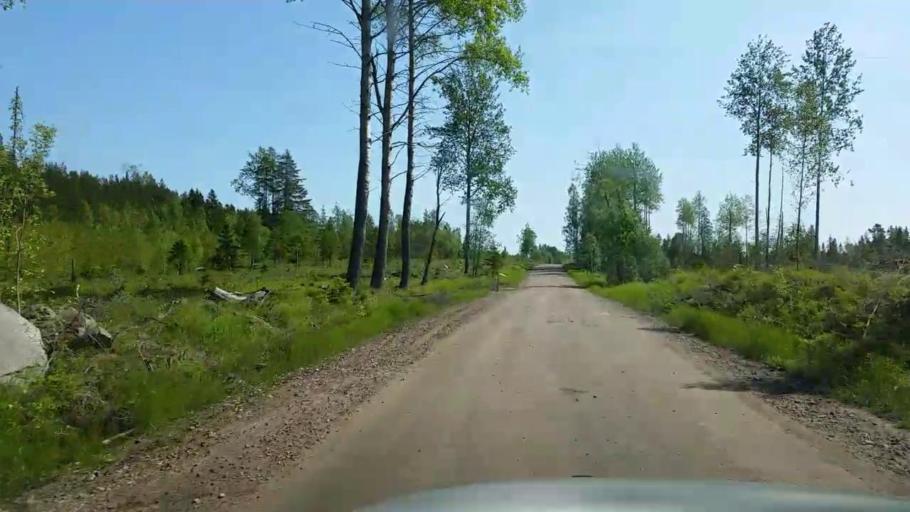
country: SE
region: Gaevleborg
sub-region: Hudiksvalls Kommun
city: Sorforsa
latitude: 61.7255
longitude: 16.9982
